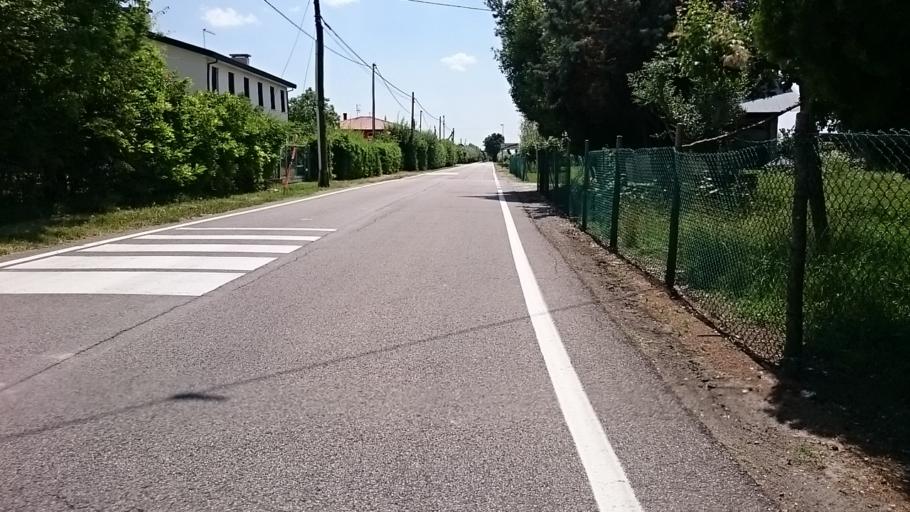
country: IT
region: Veneto
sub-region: Provincia di Padova
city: Villanova
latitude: 45.4888
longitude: 11.9771
